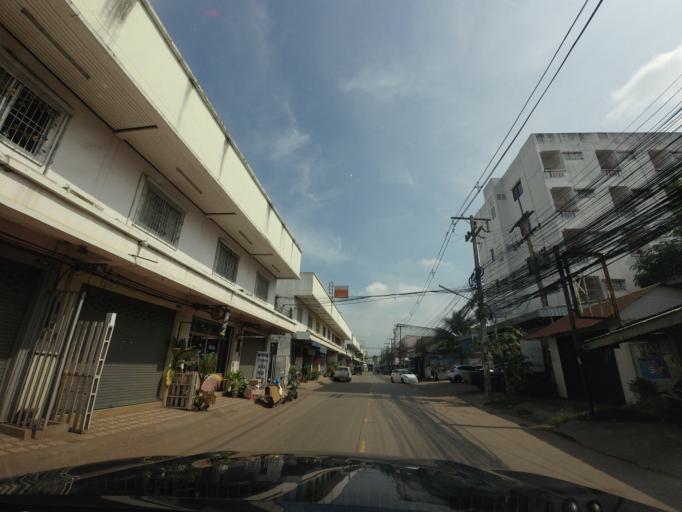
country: TH
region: Khon Kaen
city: Khon Kaen
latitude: 16.4192
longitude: 102.8237
